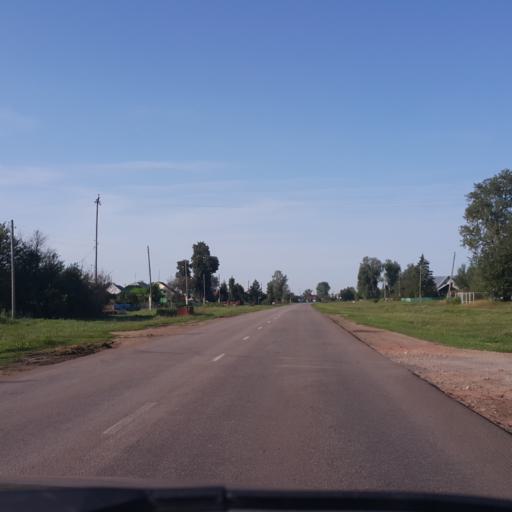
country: RU
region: Tambov
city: Novaya Lyada
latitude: 52.7797
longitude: 41.7597
